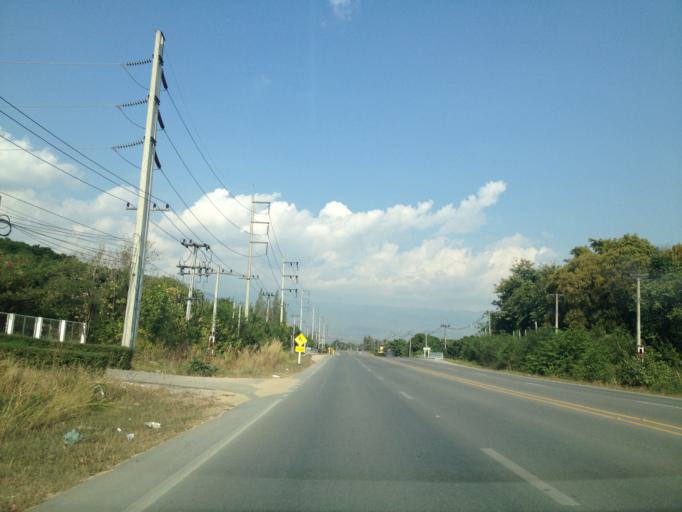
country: TH
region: Chiang Mai
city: Hot
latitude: 18.2229
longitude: 98.6138
